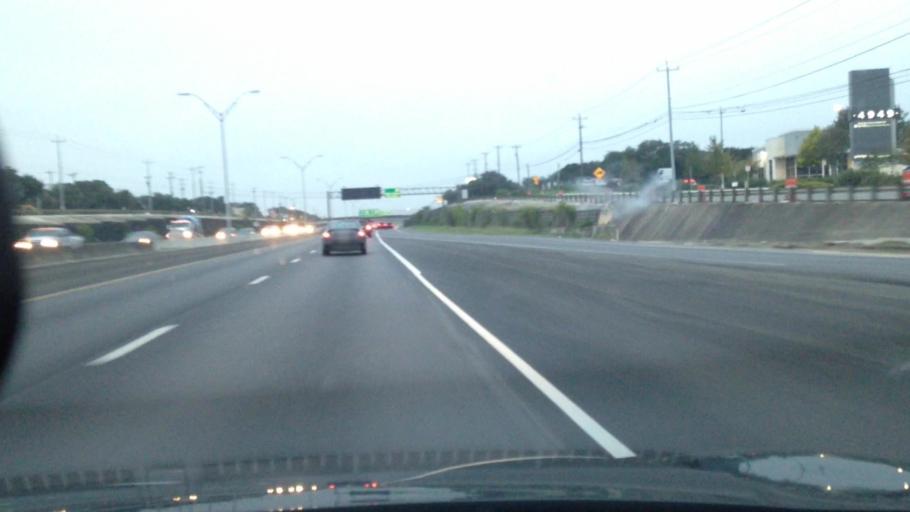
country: US
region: Texas
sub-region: Bexar County
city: Shavano Park
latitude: 29.5929
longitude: -98.5820
